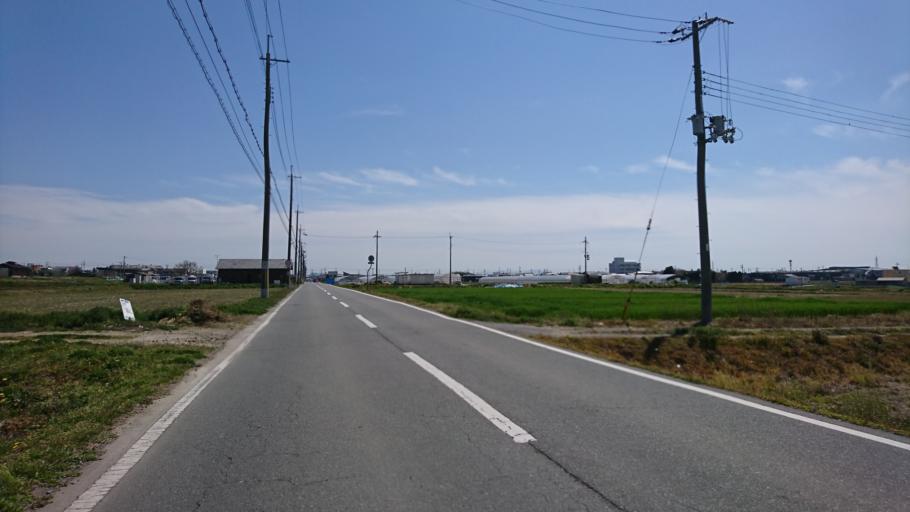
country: JP
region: Hyogo
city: Kakogawacho-honmachi
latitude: 34.7486
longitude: 134.8881
